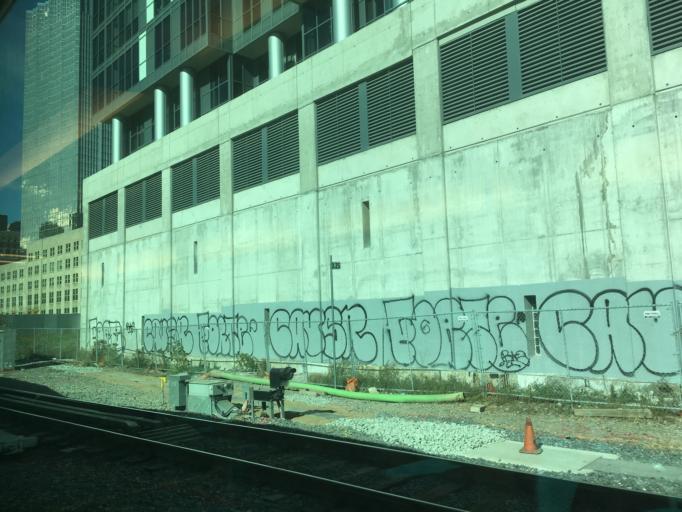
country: CA
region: Ontario
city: Toronto
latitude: 43.6457
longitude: -79.3756
